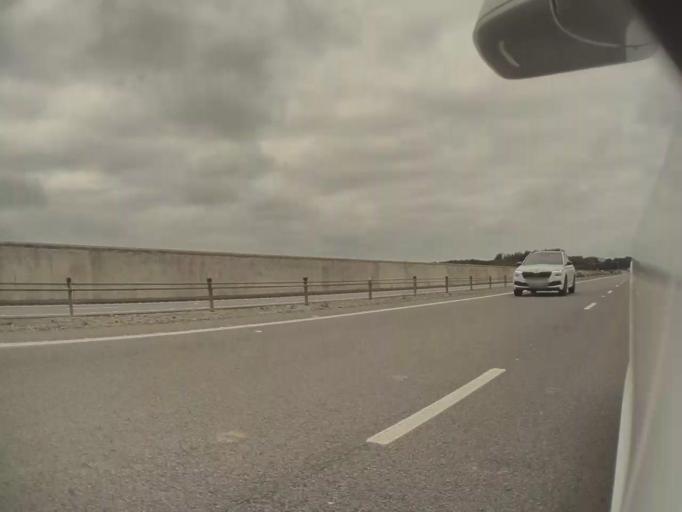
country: GB
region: Wales
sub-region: Anglesey
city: Valley
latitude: 53.2908
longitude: -4.5867
